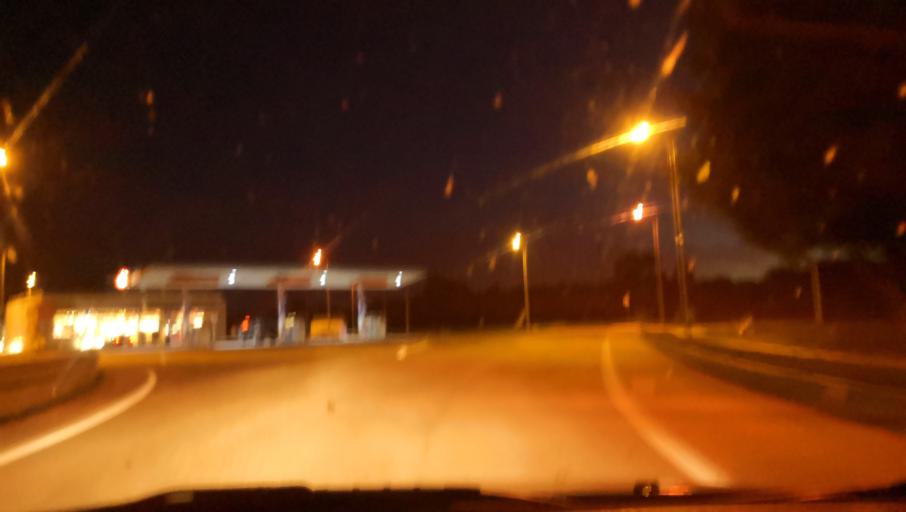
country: PT
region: Santarem
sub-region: Benavente
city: Poceirao
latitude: 38.7269
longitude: -8.6713
